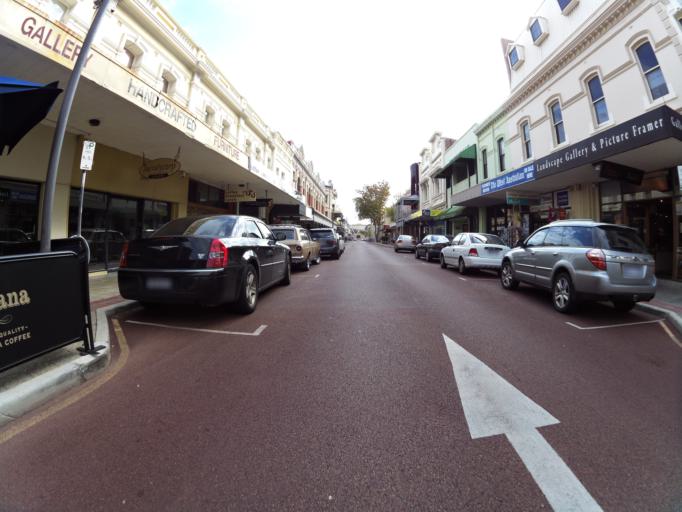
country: AU
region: Western Australia
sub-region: Fremantle
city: South Fremantle
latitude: -32.0550
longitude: 115.7449
